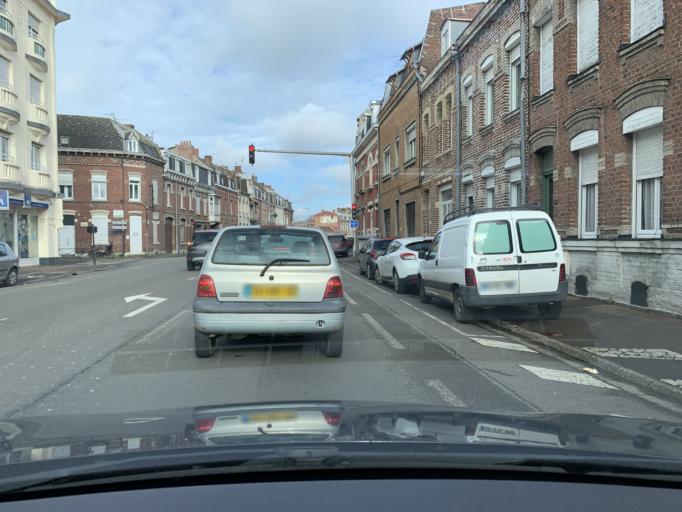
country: FR
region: Nord-Pas-de-Calais
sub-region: Departement du Nord
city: Douai
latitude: 50.3606
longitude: 3.0790
